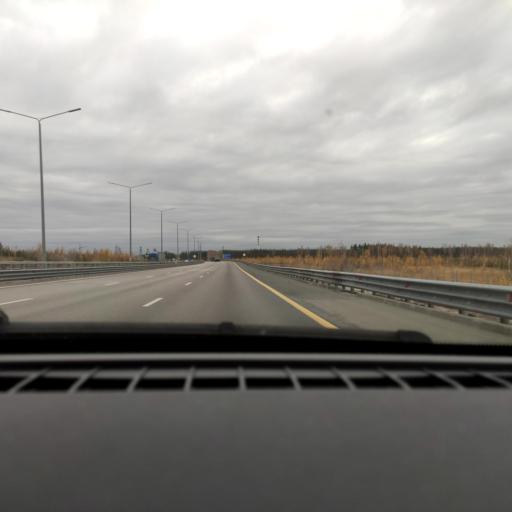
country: RU
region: Voronezj
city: Somovo
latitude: 51.7522
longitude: 39.3059
